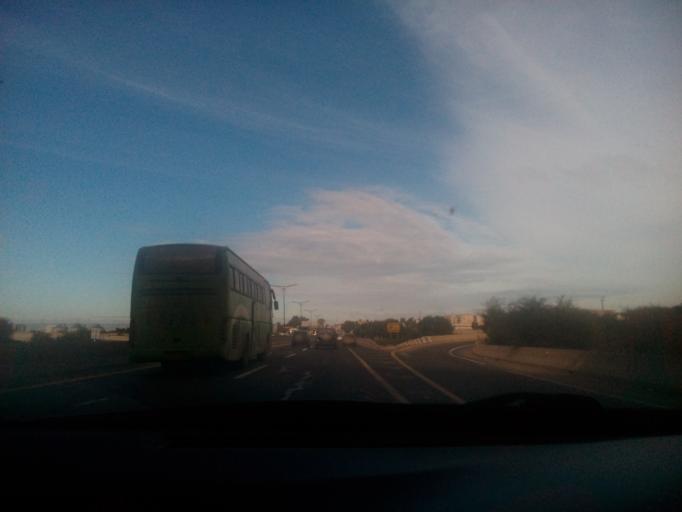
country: DZ
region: Oran
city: Es Senia
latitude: 35.6015
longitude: -0.5743
